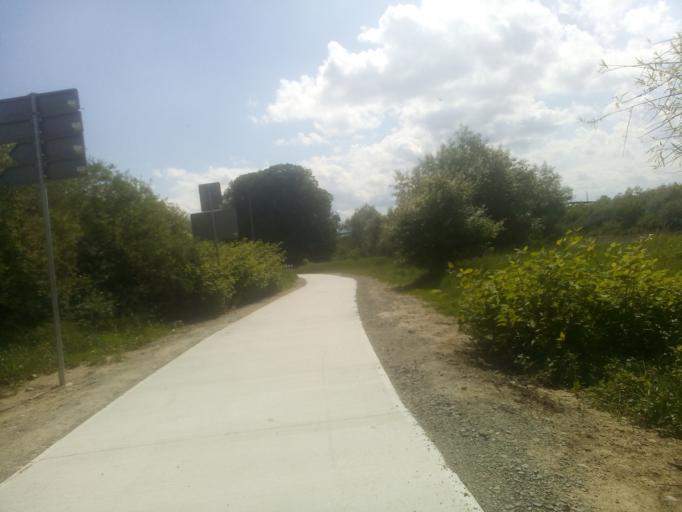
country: PL
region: Lesser Poland Voivodeship
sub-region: Powiat nowosadecki
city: Nowy Sacz
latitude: 49.6263
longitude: 20.6872
